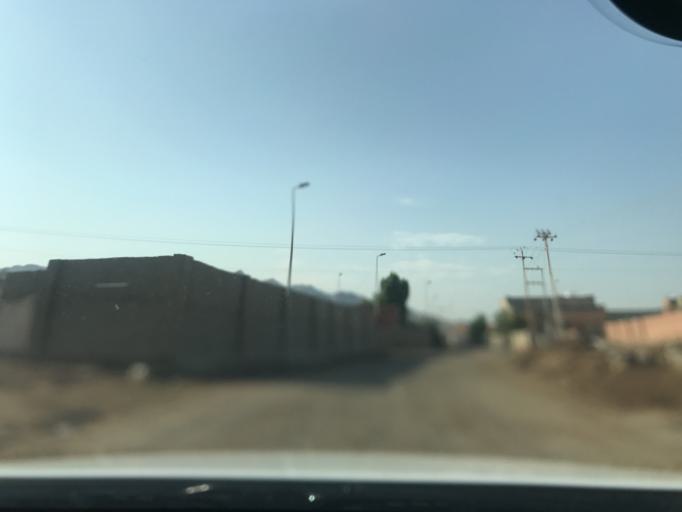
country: SA
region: Makkah
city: Al Jumum
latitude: 21.4488
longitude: 39.5346
